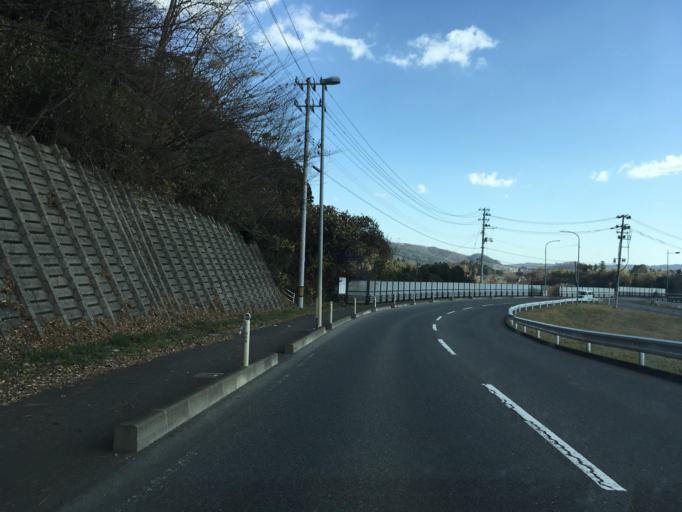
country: JP
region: Miyagi
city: Sendai
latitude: 38.2798
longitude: 140.7621
